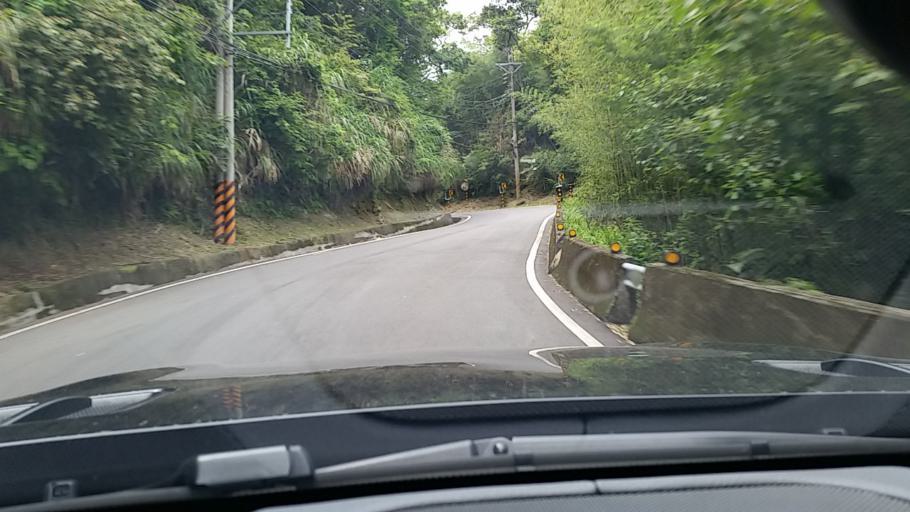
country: TW
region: Taiwan
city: Daxi
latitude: 24.7980
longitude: 121.3177
